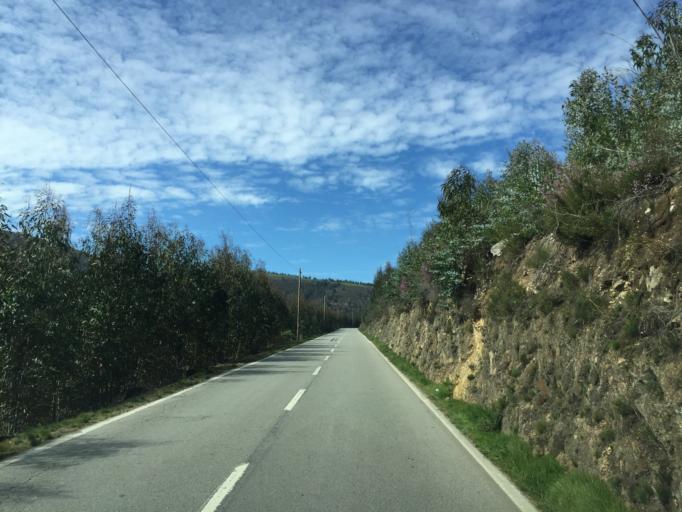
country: PT
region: Aveiro
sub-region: Arouca
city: Arouca
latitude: 40.9616
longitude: -8.2182
